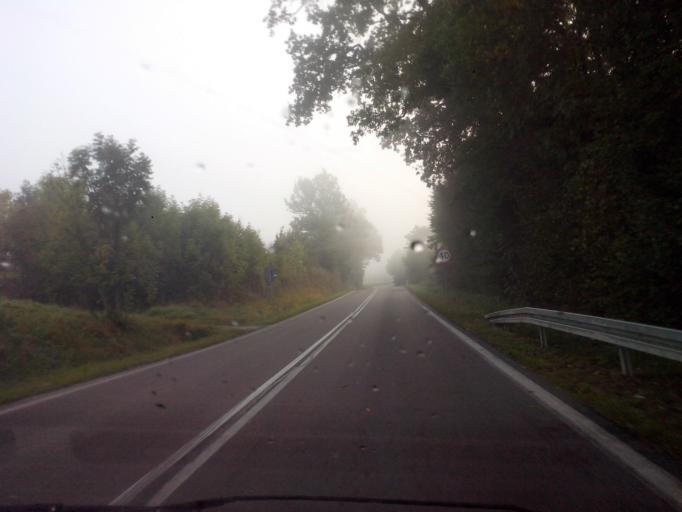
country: PL
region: Subcarpathian Voivodeship
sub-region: Powiat brzozowski
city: Domaradz
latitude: 49.8006
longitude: 21.9492
